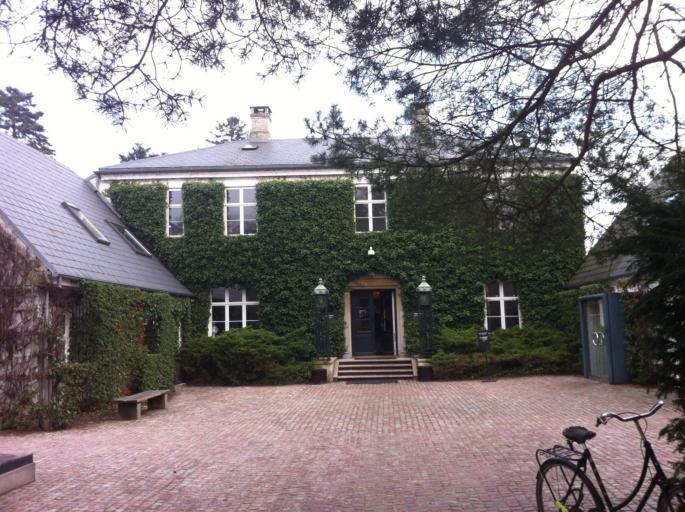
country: DK
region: Capital Region
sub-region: Fredensborg Kommune
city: Humlebaek
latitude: 55.9693
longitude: 12.5419
